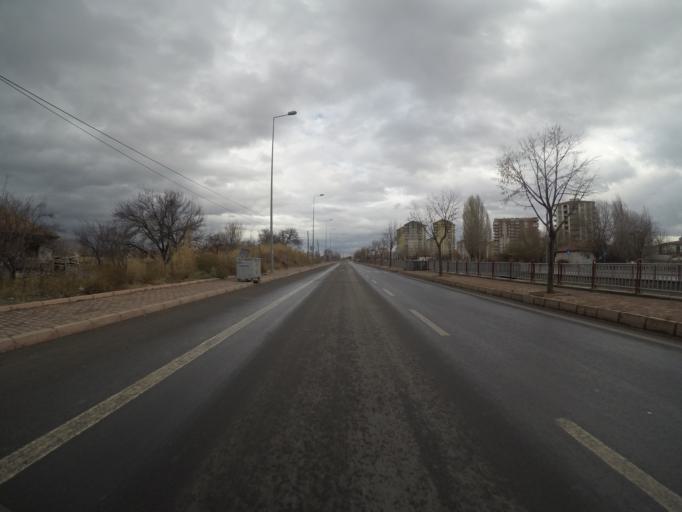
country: TR
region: Kayseri
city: Kayseri
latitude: 38.7567
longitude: 35.4800
